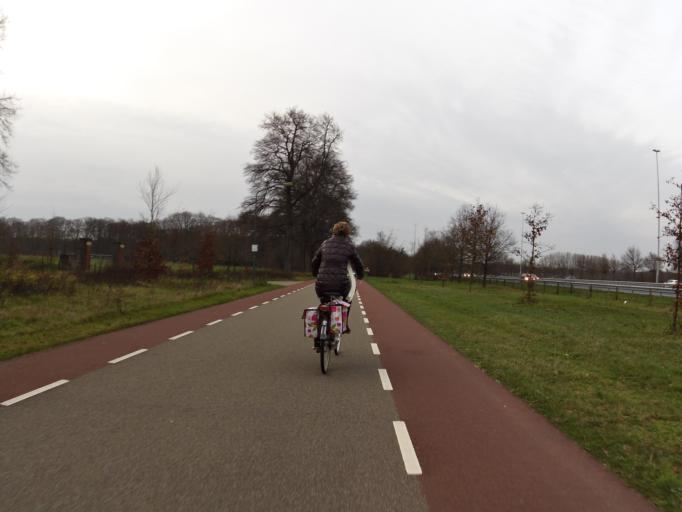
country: NL
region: North Brabant
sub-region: Gemeente Vught
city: Vught
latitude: 51.6339
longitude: 5.3111
